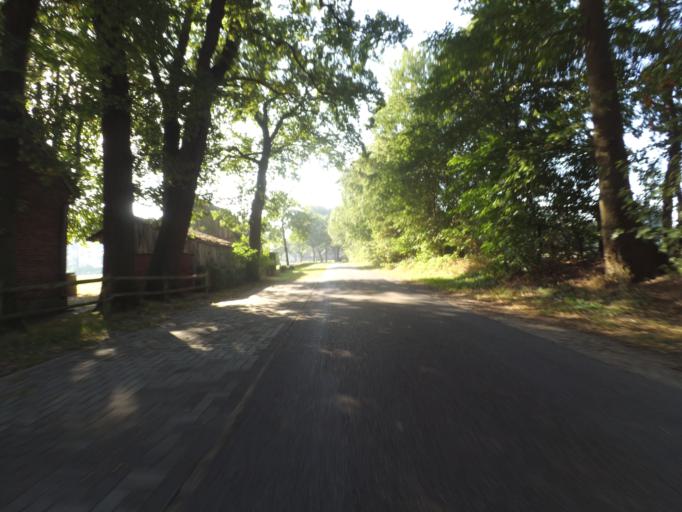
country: DE
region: Lower Saxony
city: Ohne
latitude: 52.2713
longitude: 7.2711
